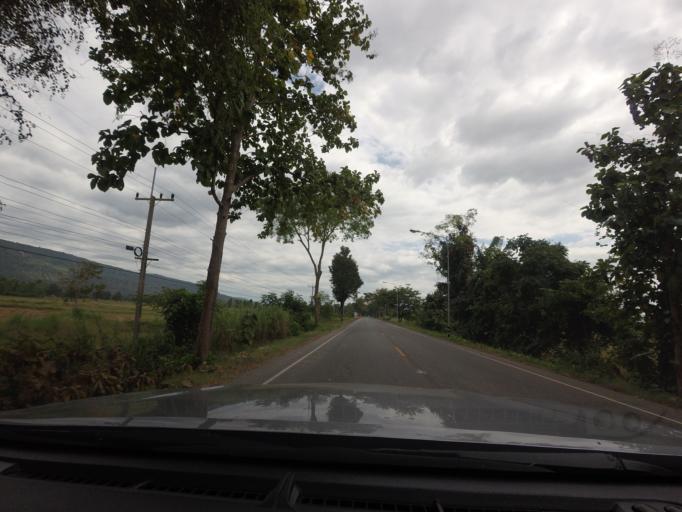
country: TH
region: Phitsanulok
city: Wang Thong
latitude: 16.7062
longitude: 100.4944
